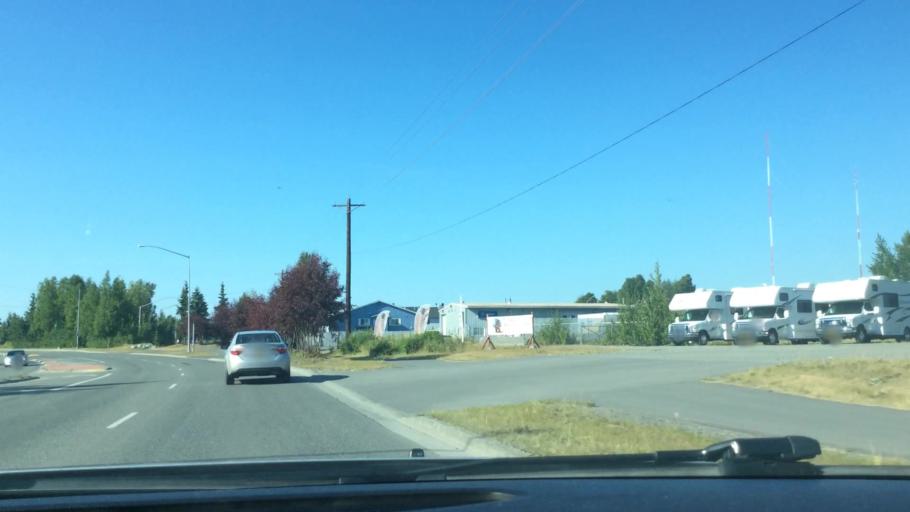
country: US
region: Alaska
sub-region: Anchorage Municipality
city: Anchorage
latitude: 61.1614
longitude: -149.8340
